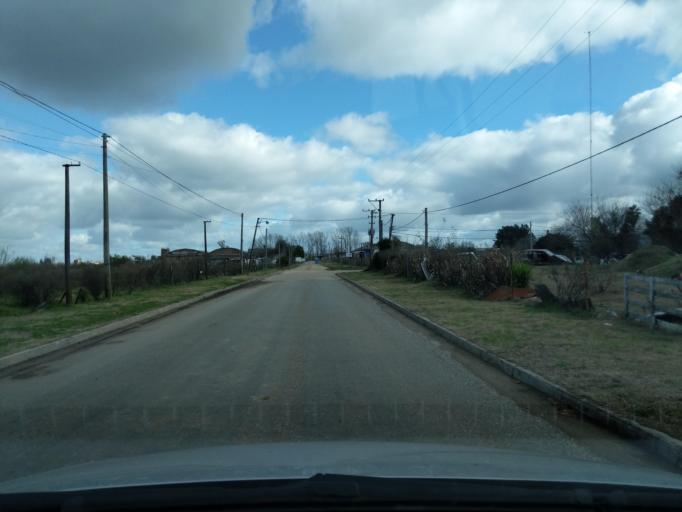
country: UY
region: Florida
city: Florida
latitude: -34.1093
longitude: -56.2204
